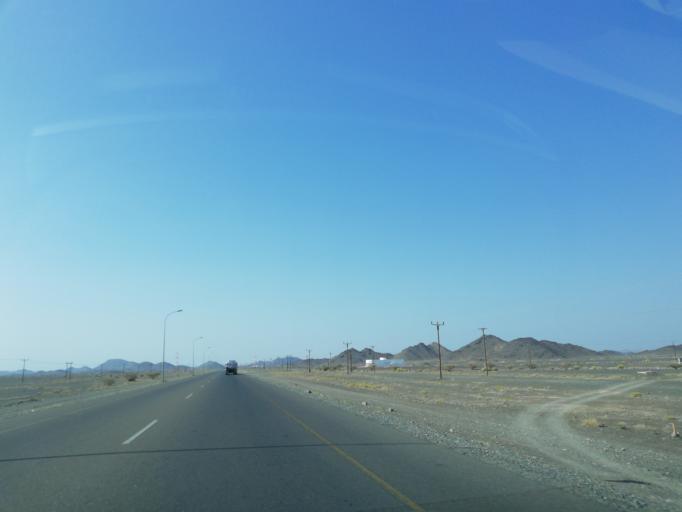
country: OM
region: Ash Sharqiyah
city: Ibra'
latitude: 22.7588
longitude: 58.1464
